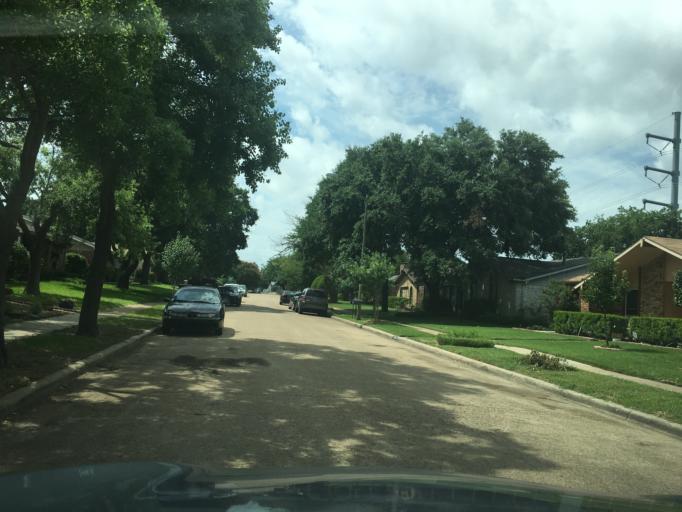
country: US
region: Texas
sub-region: Dallas County
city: Richardson
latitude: 32.9123
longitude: -96.7084
